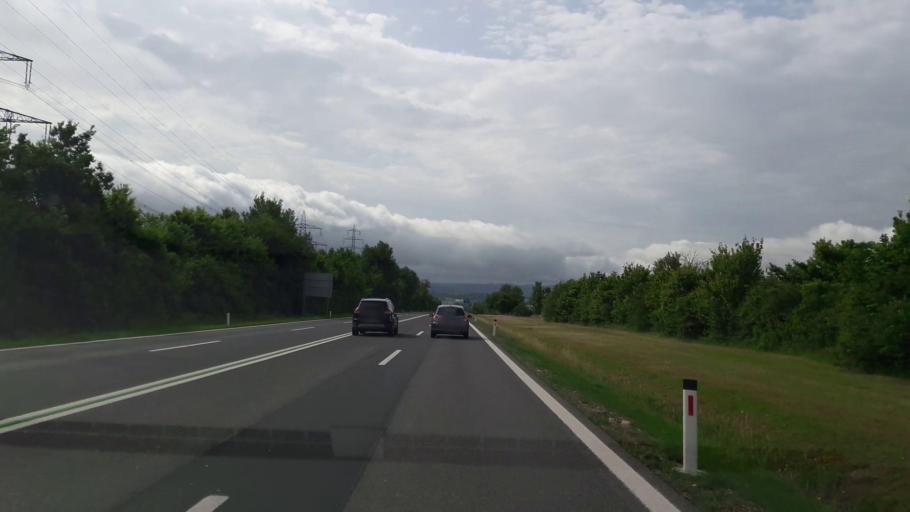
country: AT
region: Burgenland
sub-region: Politischer Bezirk Oberpullendorf
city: Kobersdorf
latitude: 47.5973
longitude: 16.4058
